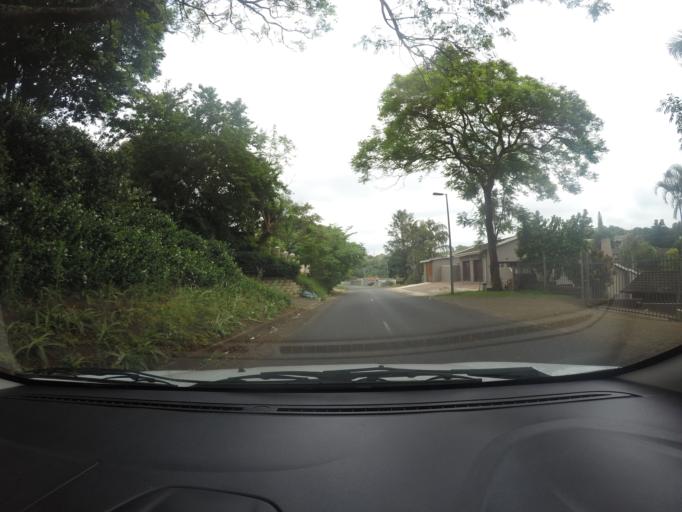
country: ZA
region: KwaZulu-Natal
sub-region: uThungulu District Municipality
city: Empangeni
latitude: -28.7500
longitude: 31.8896
